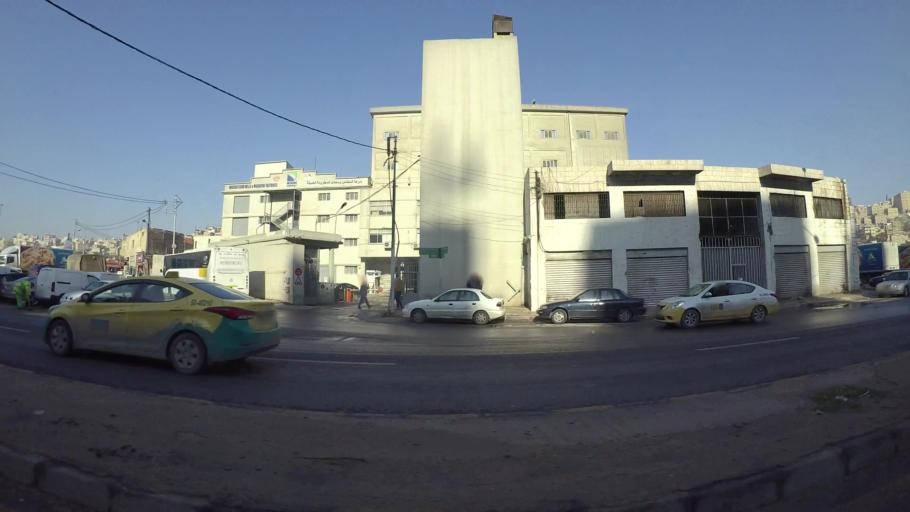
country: JO
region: Amman
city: Amman
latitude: 31.9646
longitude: 35.9630
